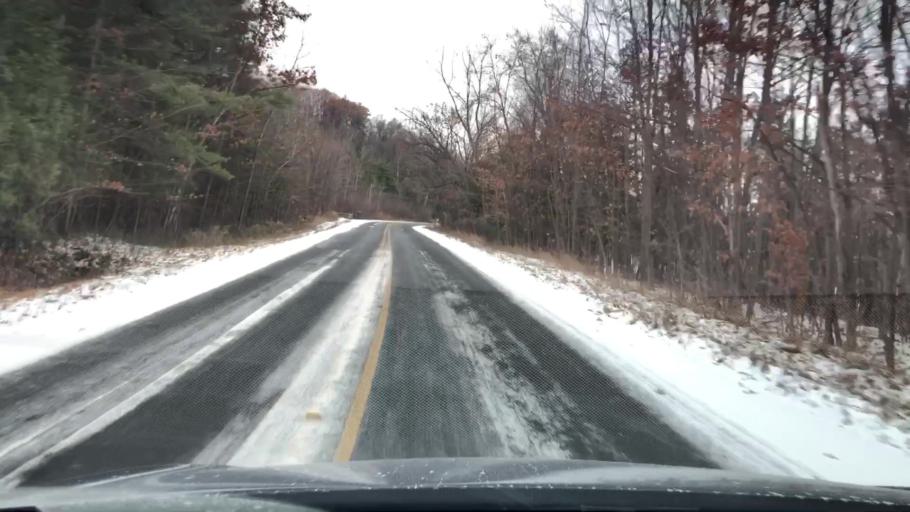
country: US
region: Michigan
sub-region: Leelanau County
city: Greilickville
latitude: 44.8330
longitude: -85.5634
